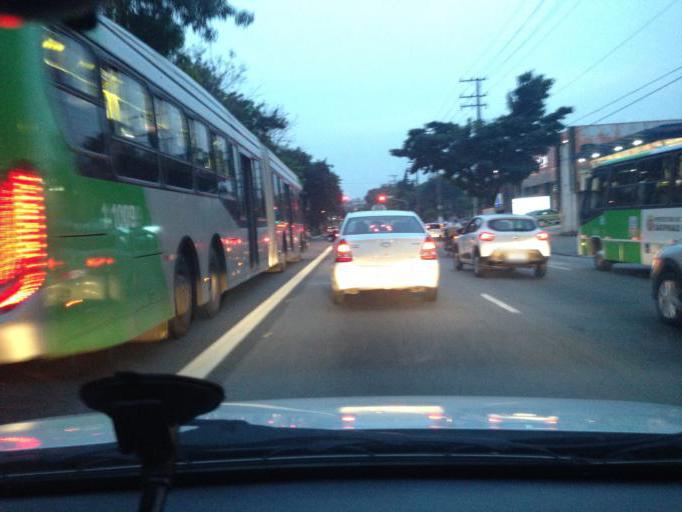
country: BR
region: Sao Paulo
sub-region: Sao Paulo
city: Sao Paulo
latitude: -23.4997
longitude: -46.7066
